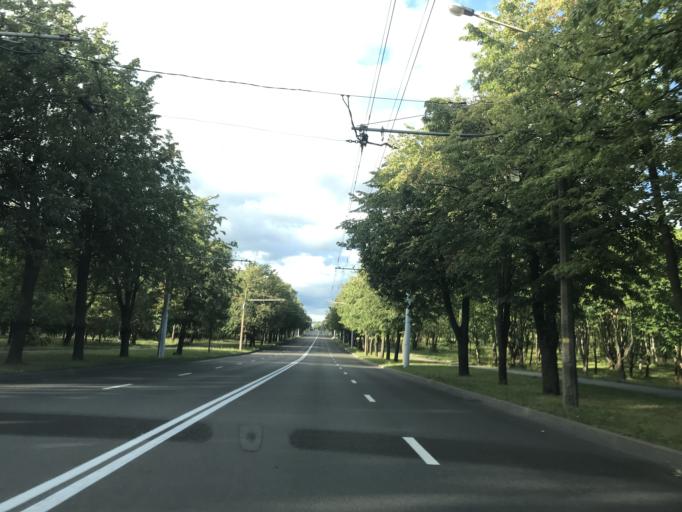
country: BY
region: Minsk
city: Minsk
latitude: 53.9407
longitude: 27.6178
